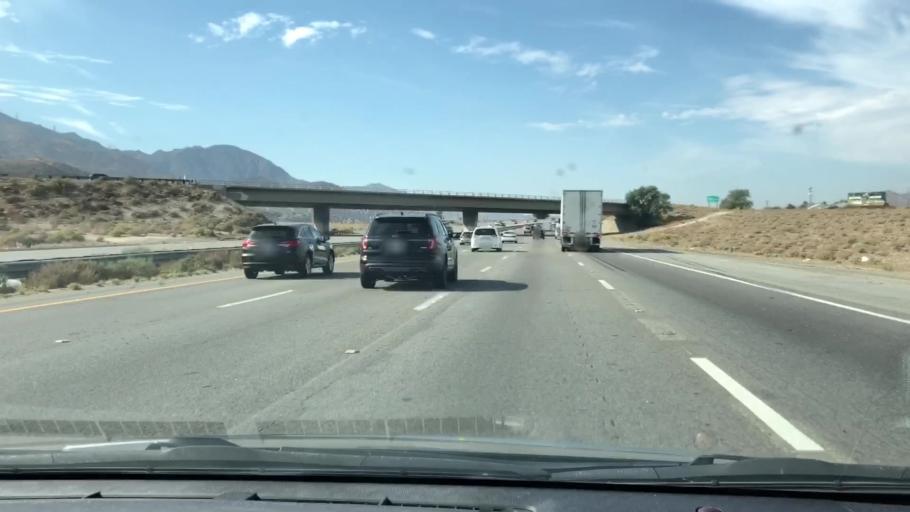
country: US
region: California
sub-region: Riverside County
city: Cabazon
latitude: 33.9228
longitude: -116.6764
